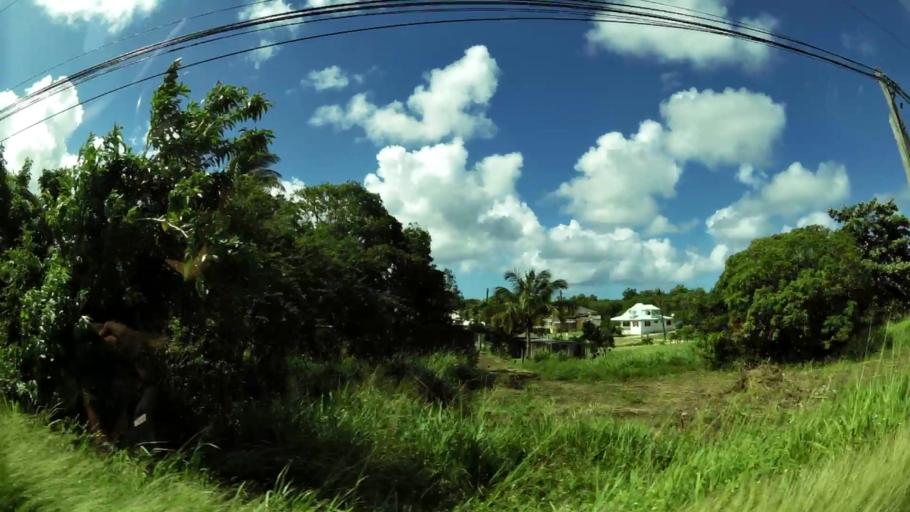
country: GP
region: Guadeloupe
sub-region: Guadeloupe
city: Anse-Bertrand
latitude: 16.4532
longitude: -61.4785
